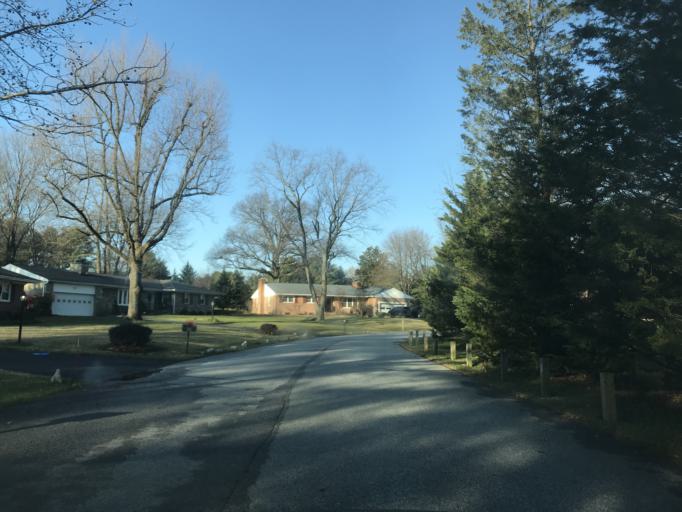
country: US
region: Maryland
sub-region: Baltimore County
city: Towson
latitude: 39.3886
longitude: -76.5861
